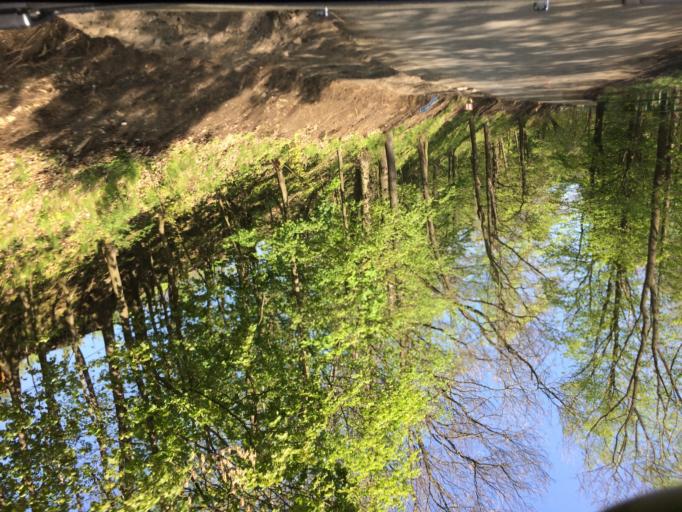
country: PL
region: Lower Silesian Voivodeship
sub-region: Powiat dzierzoniowski
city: Pieszyce
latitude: 50.6877
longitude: 16.5493
